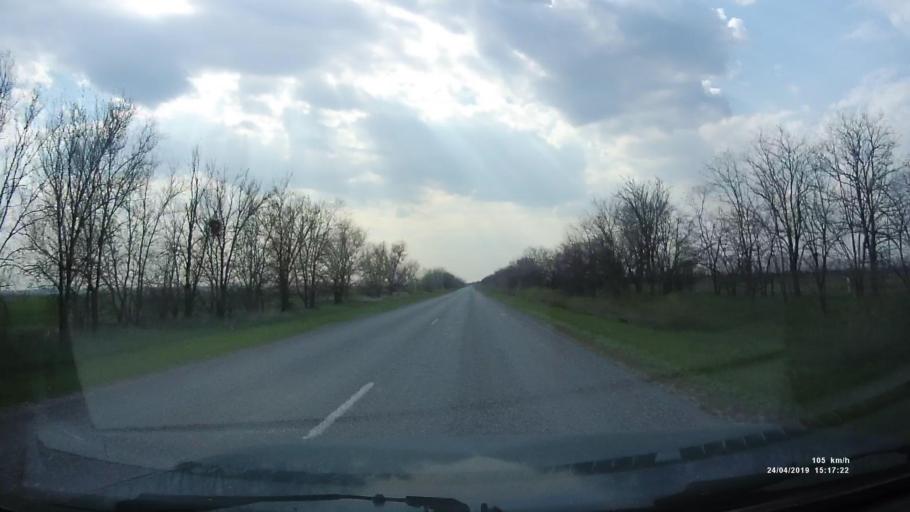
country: RU
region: Rostov
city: Remontnoye
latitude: 46.5465
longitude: 43.1910
